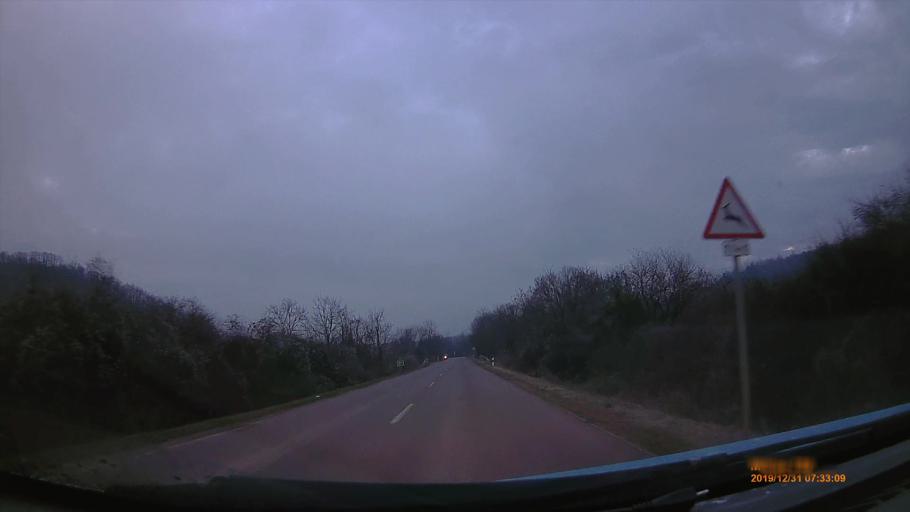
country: HU
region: Heves
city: Recsk
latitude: 47.9269
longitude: 20.1314
